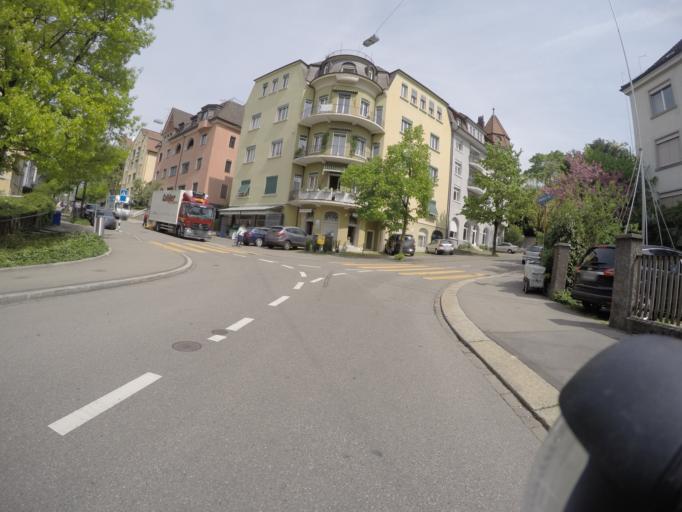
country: CH
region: Zurich
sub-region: Bezirk Zuerich
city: Zuerich (Kreis 6) / Oberstrass
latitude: 47.3860
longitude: 8.5456
